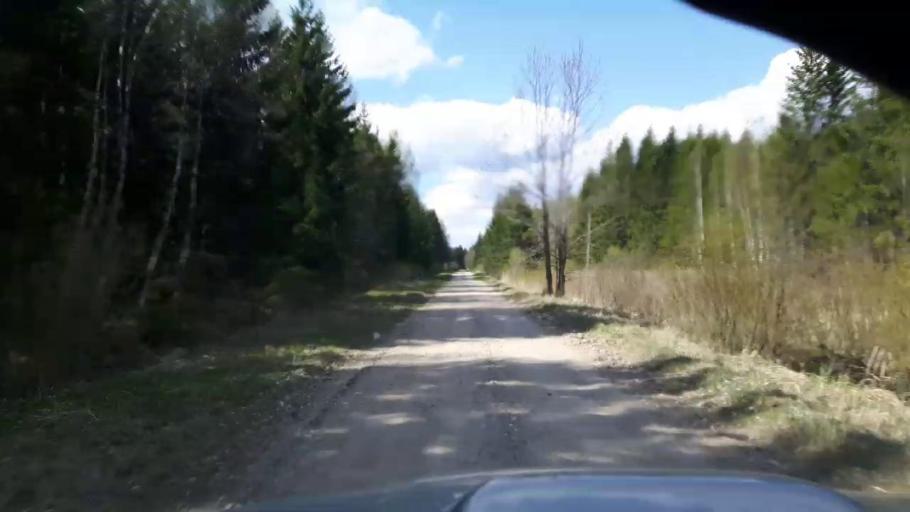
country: EE
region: Paernumaa
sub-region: Tootsi vald
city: Tootsi
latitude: 58.4451
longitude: 24.9121
